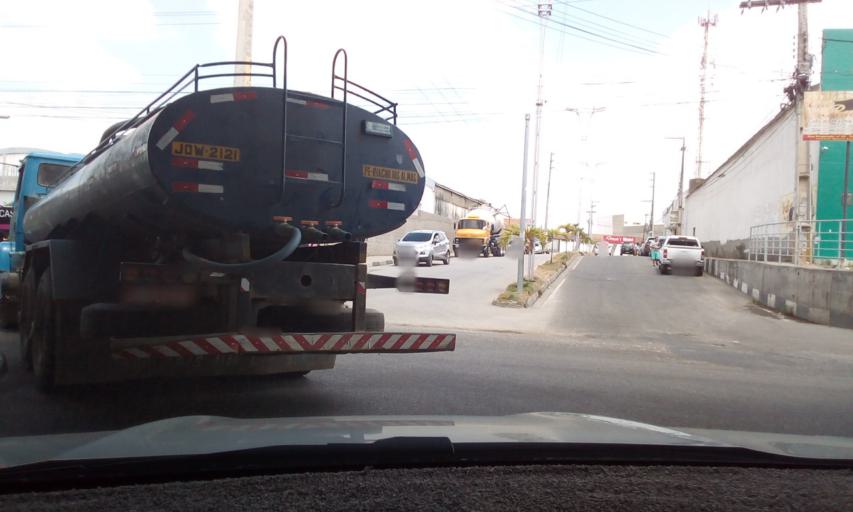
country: BR
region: Pernambuco
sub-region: Caruaru
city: Caruaru
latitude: -8.2671
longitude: -35.9787
